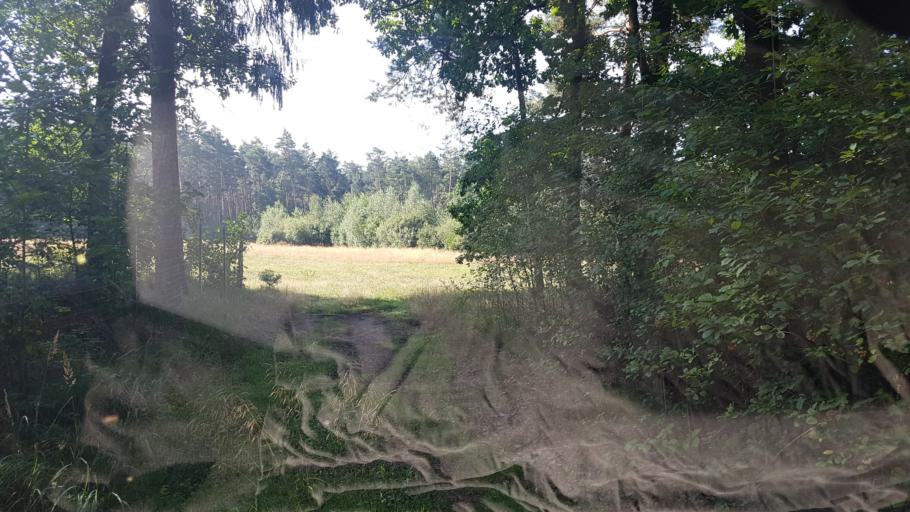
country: DE
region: Brandenburg
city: Finsterwalde
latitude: 51.5912
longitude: 13.6854
